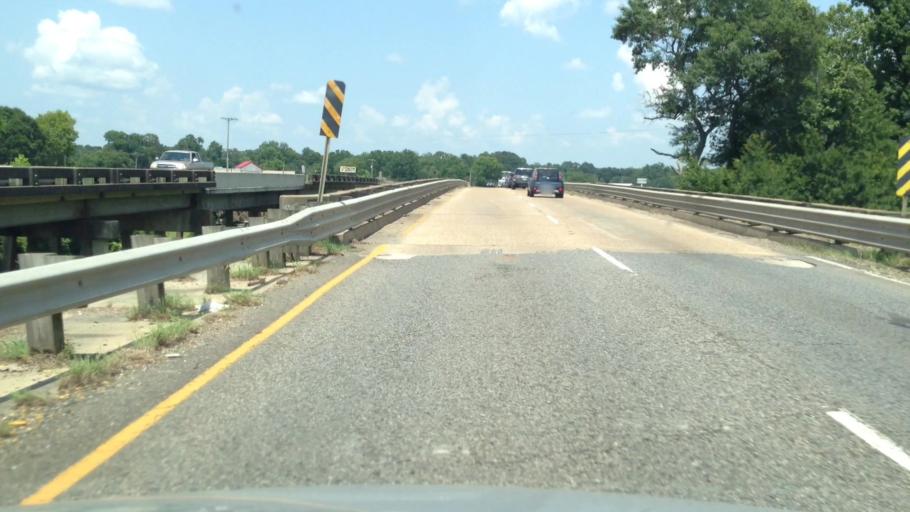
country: US
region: Louisiana
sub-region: Saint Landry Parish
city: Opelousas
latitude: 30.5352
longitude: -92.0595
